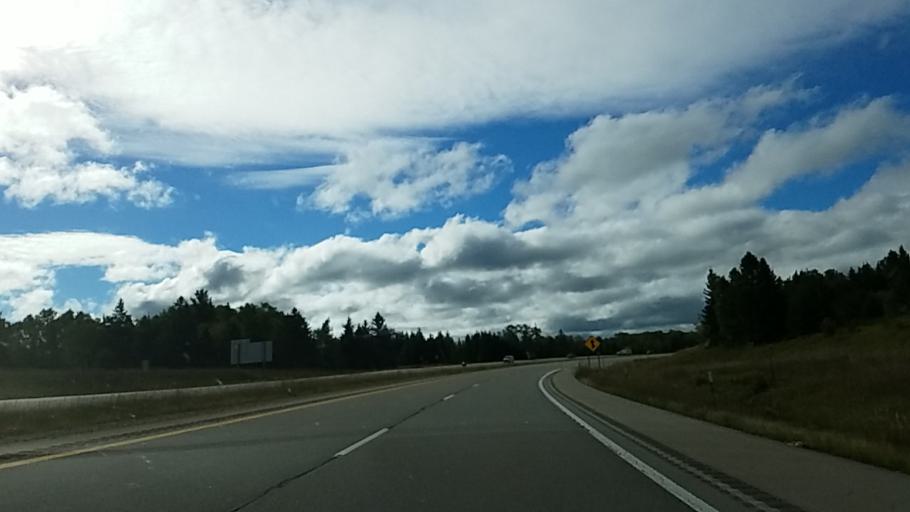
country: US
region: Michigan
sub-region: Mackinac County
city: Saint Ignace
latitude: 45.7612
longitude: -84.7304
